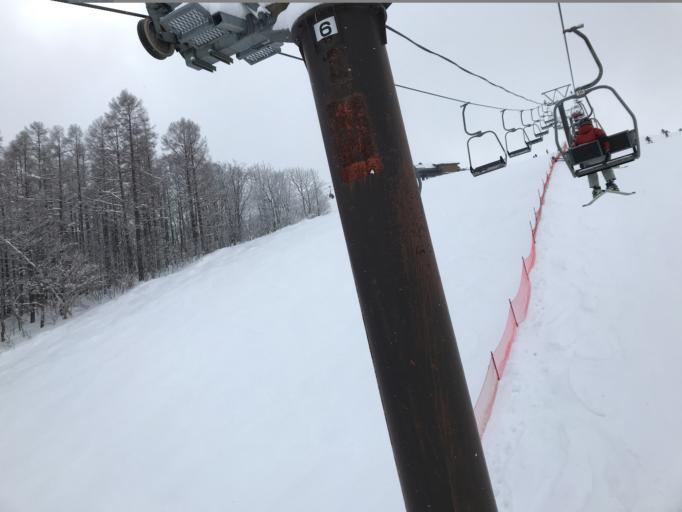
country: JP
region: Nagano
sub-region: Kitaazumi Gun
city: Hakuba
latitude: 36.7114
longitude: 137.8203
